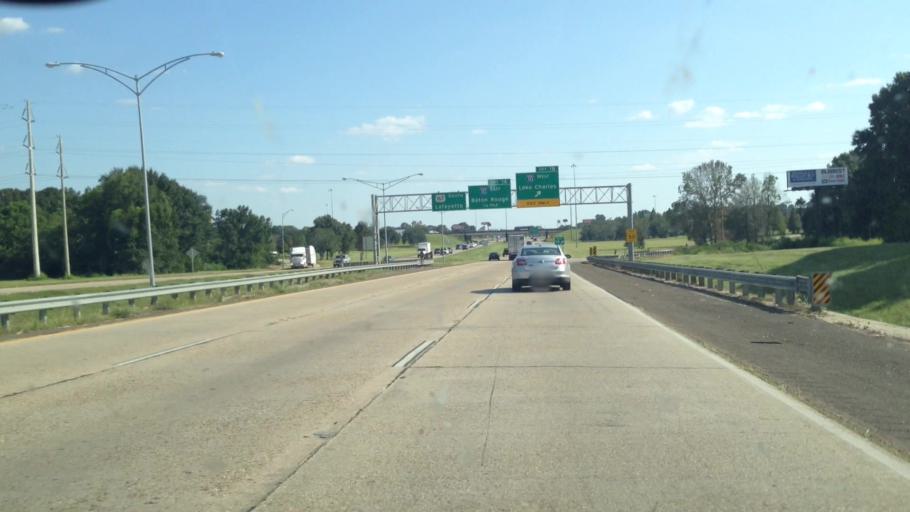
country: US
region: Louisiana
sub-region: Lafayette Parish
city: Lafayette
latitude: 30.2650
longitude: -92.0171
